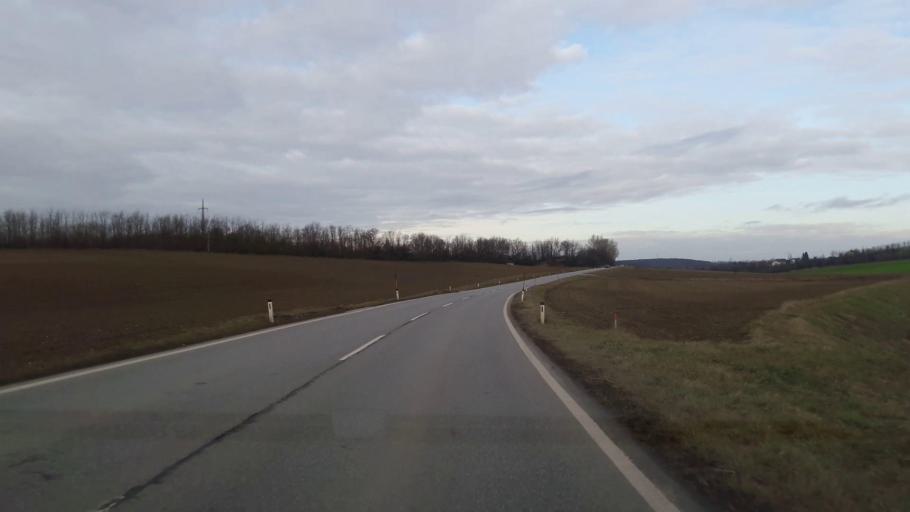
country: AT
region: Lower Austria
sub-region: Politischer Bezirk Mistelbach
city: Asparn an der Zaya
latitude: 48.6138
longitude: 16.5277
